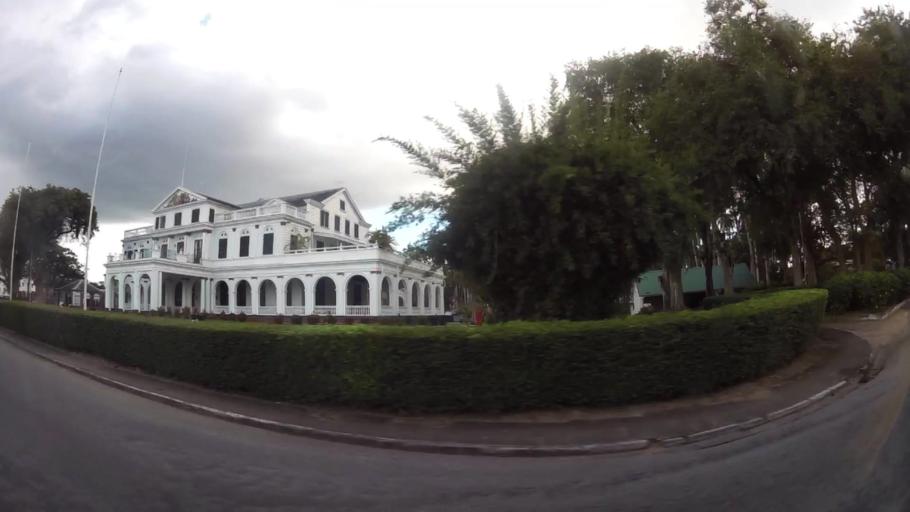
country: SR
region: Paramaribo
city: Paramaribo
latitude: 5.8263
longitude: -55.1510
